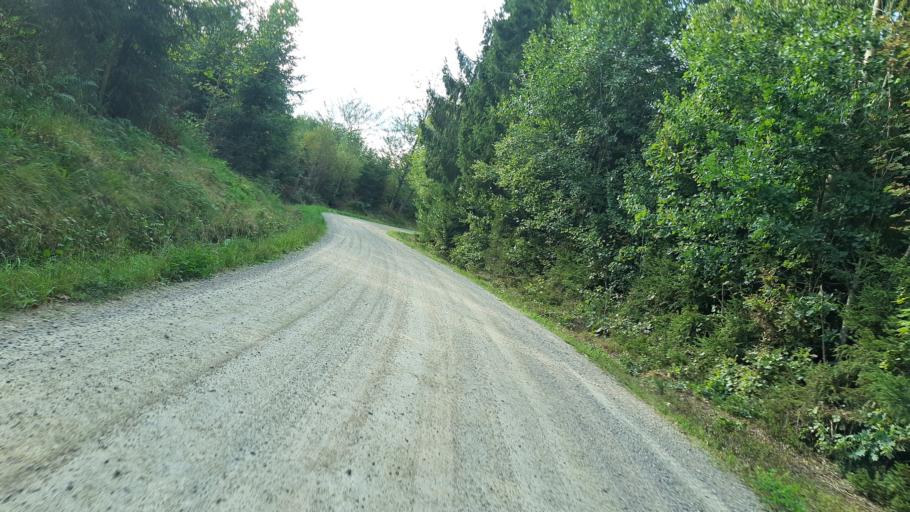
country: SE
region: Blekinge
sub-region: Ronneby Kommun
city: Kallinge
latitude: 56.2547
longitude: 15.3471
